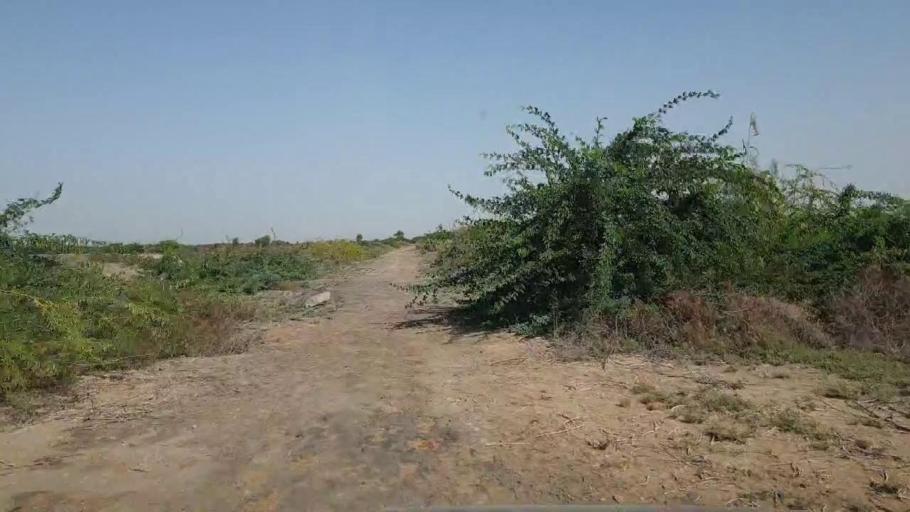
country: PK
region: Sindh
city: Tando Bago
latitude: 24.7157
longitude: 69.0722
